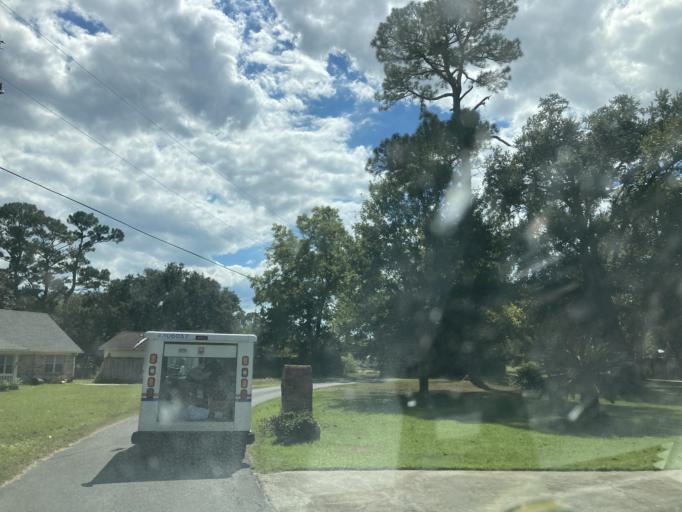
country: US
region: Mississippi
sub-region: Jackson County
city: Gulf Hills
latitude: 30.4414
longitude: -88.8503
